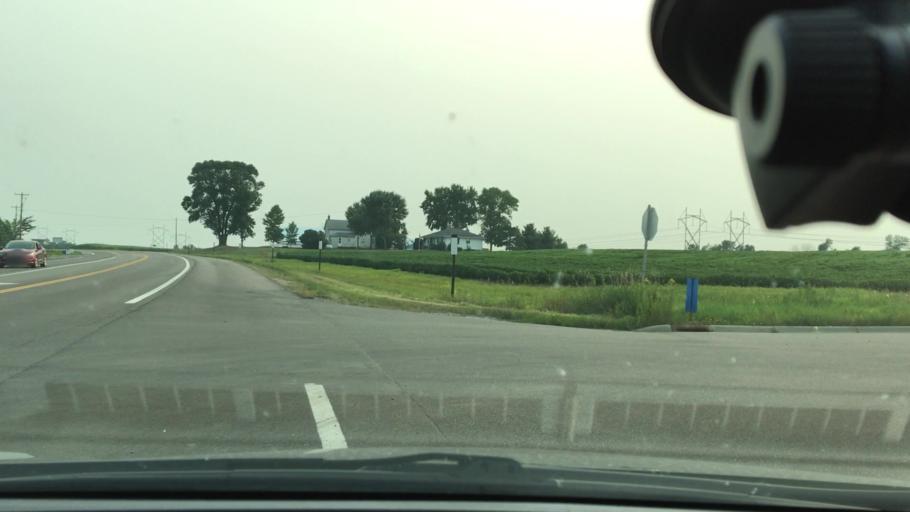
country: US
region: Minnesota
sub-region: Wright County
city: Saint Michael
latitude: 45.2025
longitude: -93.6814
